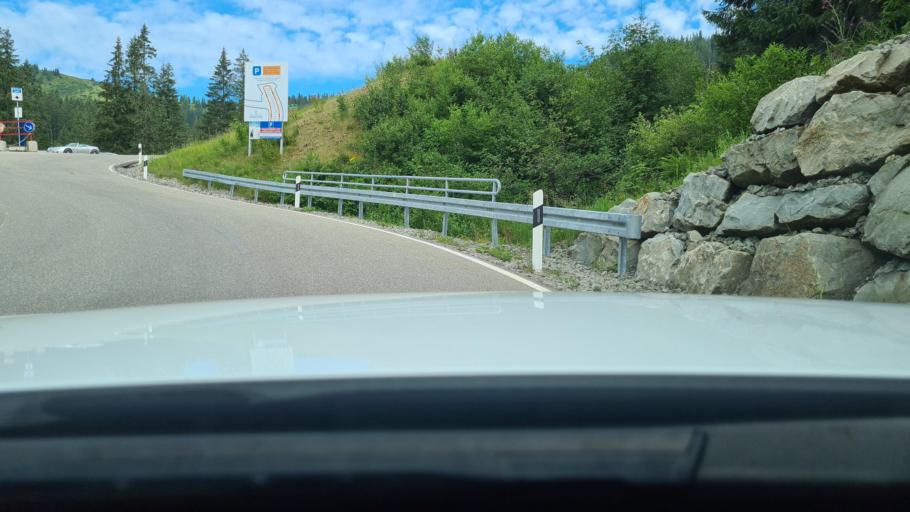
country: DE
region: Bavaria
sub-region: Swabia
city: Obermaiselstein
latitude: 47.4408
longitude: 10.1766
